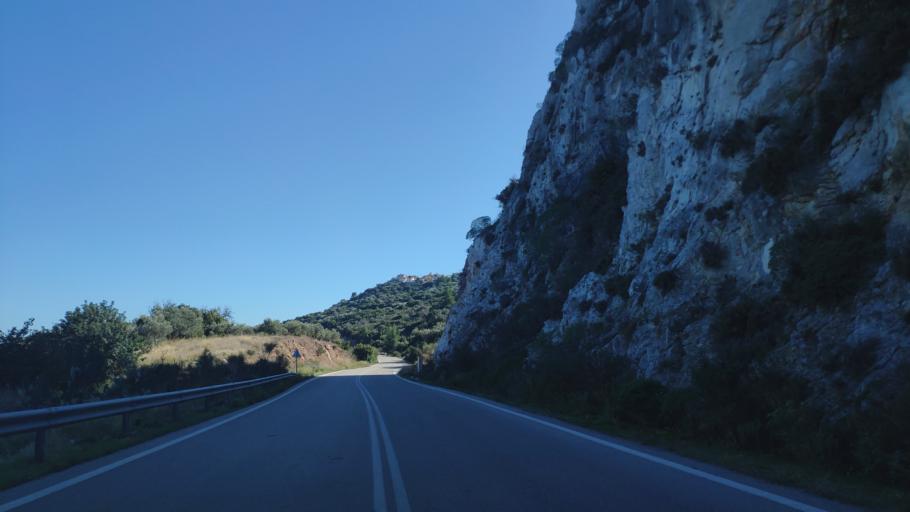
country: GR
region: Peloponnese
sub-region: Nomos Argolidos
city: Palaia Epidavros
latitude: 37.5815
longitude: 23.2338
